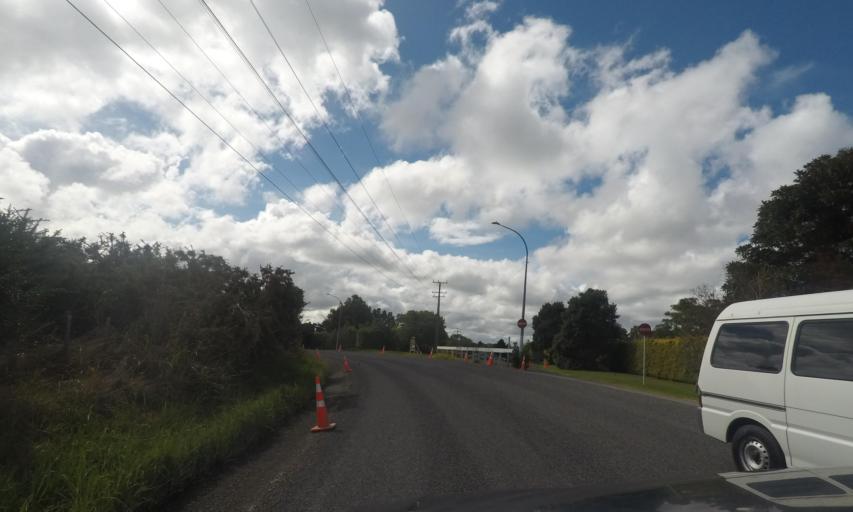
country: NZ
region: Auckland
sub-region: Auckland
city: Rosebank
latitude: -36.7931
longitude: 174.6374
